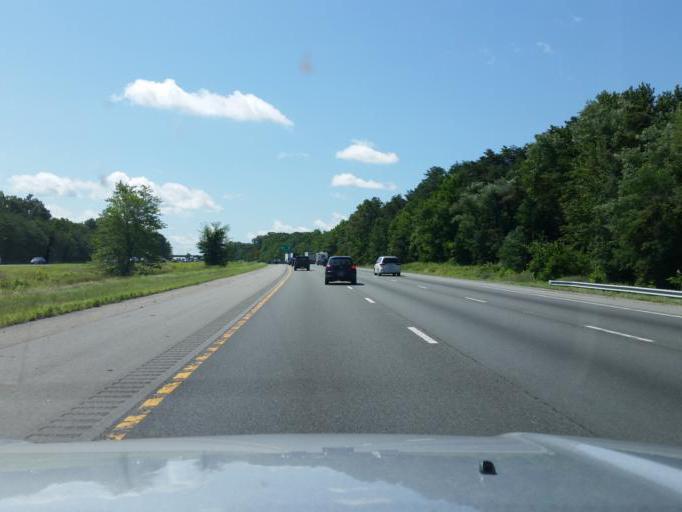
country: US
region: Virginia
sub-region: City of Fredericksburg
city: Fredericksburg
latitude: 38.2571
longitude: -77.5132
